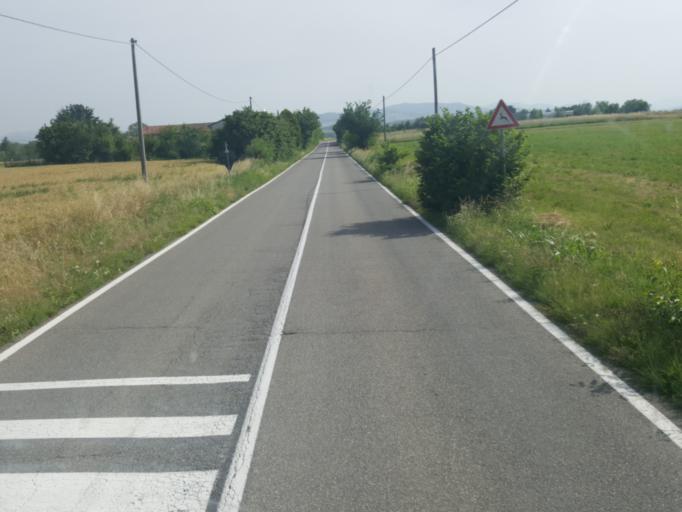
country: IT
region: Emilia-Romagna
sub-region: Provincia di Piacenza
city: Niviano
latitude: 44.9386
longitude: 9.6415
